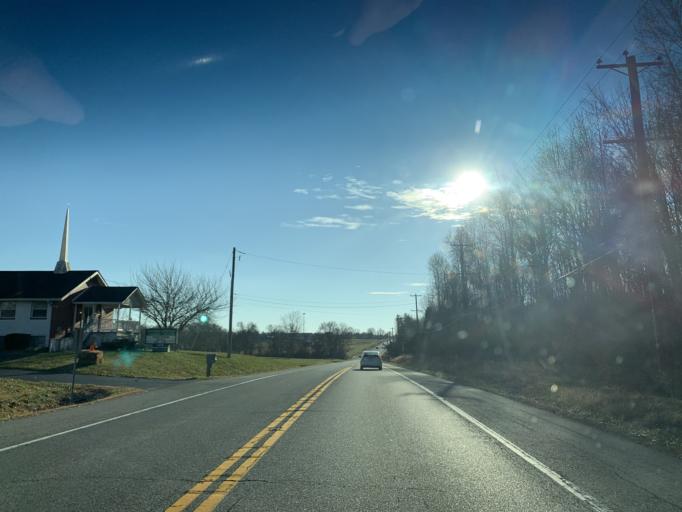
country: US
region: Maryland
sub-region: Cecil County
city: Elkton
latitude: 39.5002
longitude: -75.8368
